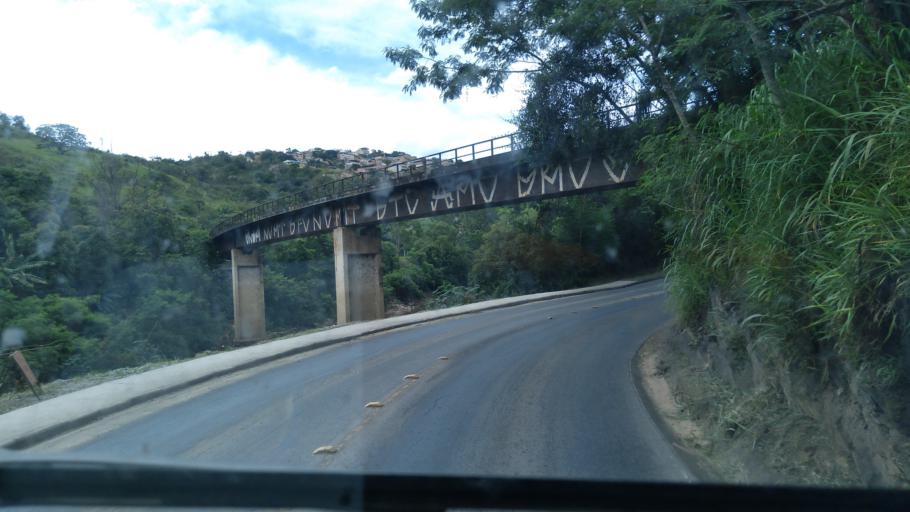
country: BR
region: Minas Gerais
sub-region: Belo Horizonte
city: Belo Horizonte
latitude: -19.8758
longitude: -43.8582
